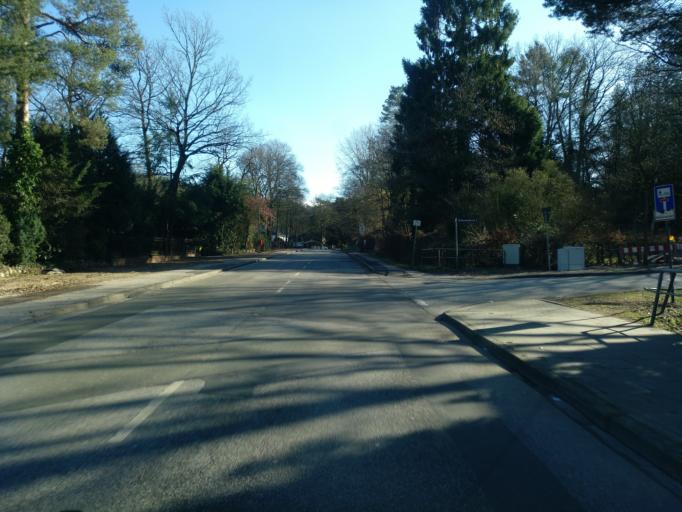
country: DE
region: Lower Saxony
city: Neu Wulmstorf
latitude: 53.4656
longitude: 9.8904
